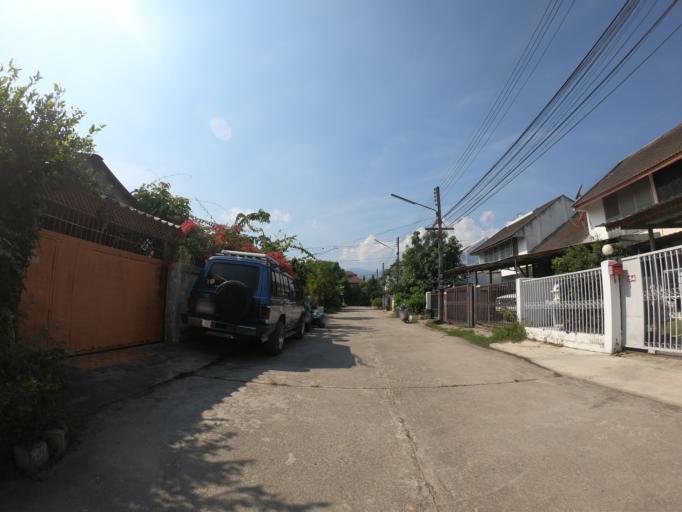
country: TH
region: Chiang Mai
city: Chiang Mai
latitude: 18.8080
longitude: 98.9997
